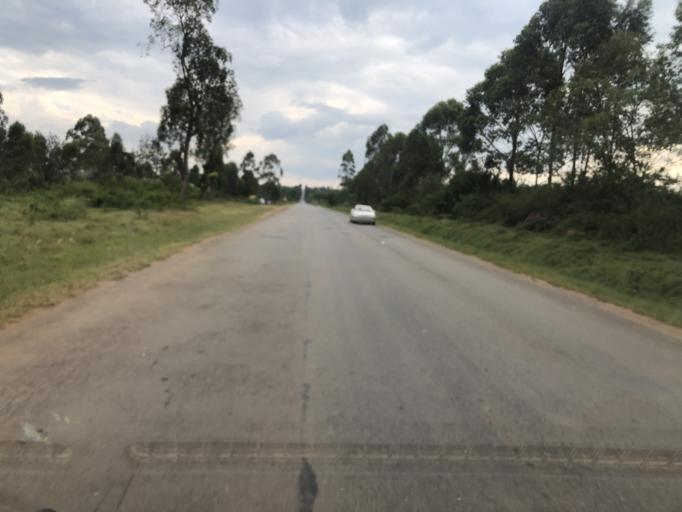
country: UG
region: Western Region
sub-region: Sheema District
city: Kibingo
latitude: -0.5793
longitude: 30.4226
